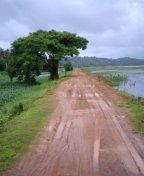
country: IN
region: Kerala
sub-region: Thrissur District
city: Trichur
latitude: 10.4780
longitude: 76.2111
